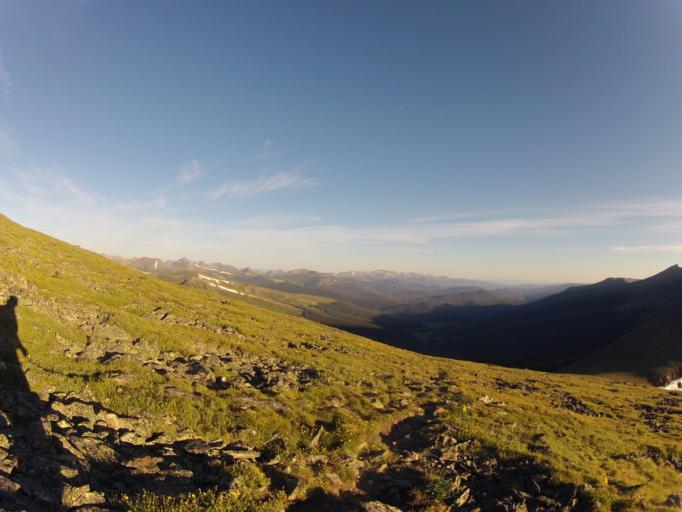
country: US
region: Colorado
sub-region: Larimer County
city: Estes Park
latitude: 40.4349
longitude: -105.7020
